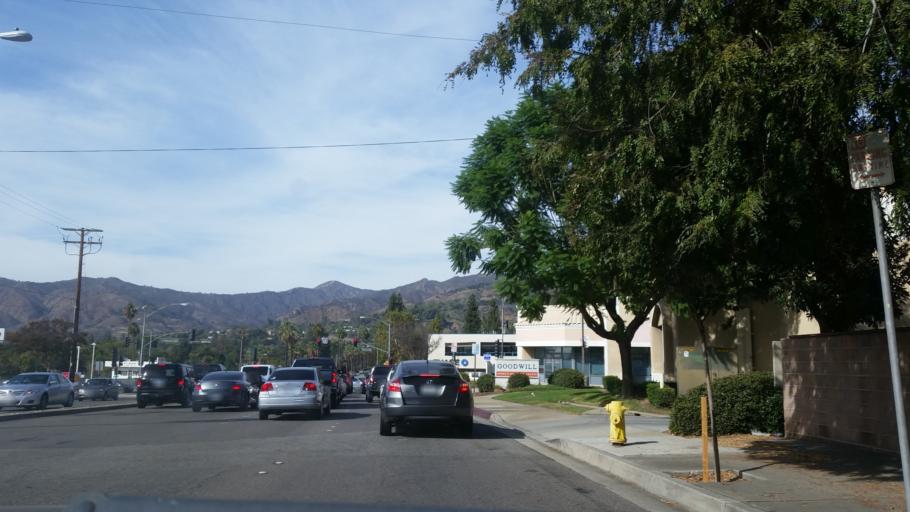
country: US
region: California
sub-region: Los Angeles County
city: Charter Oak
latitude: 34.1276
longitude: -117.8288
